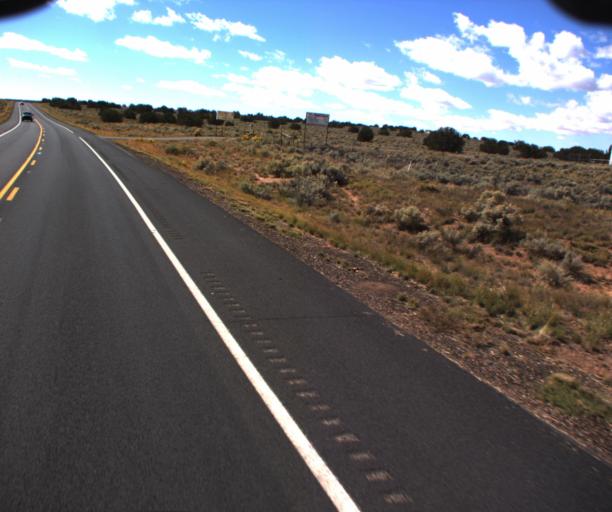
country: US
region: Arizona
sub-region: Apache County
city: Houck
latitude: 35.1811
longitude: -109.3376
